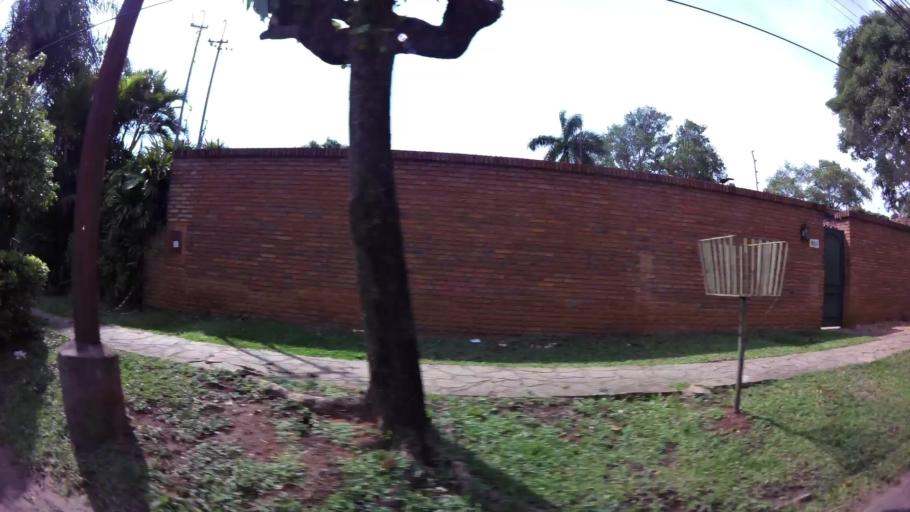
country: PY
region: Asuncion
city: Asuncion
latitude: -25.2674
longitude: -57.5618
